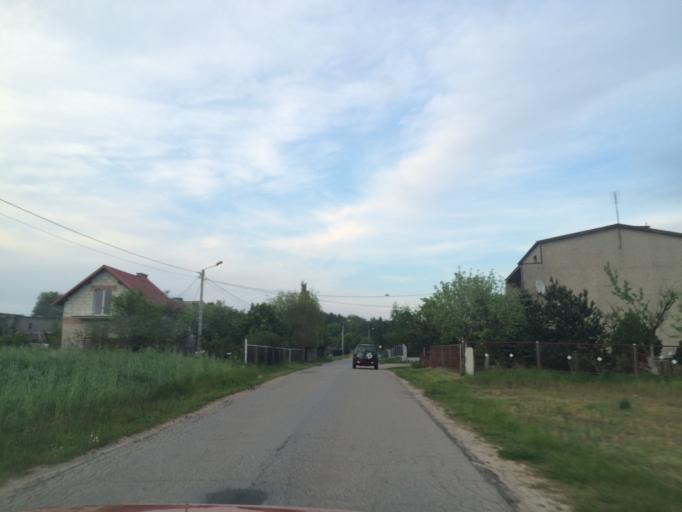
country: PL
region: Warmian-Masurian Voivodeship
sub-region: Powiat nowomiejski
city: Kurzetnik
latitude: 53.4019
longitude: 19.5449
